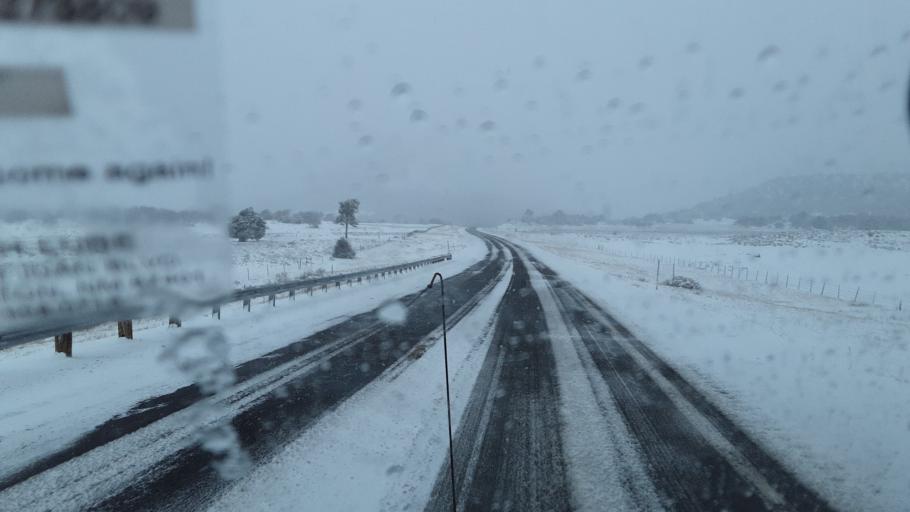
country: US
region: New Mexico
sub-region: Rio Arriba County
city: Dulce
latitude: 36.9459
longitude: -106.7897
